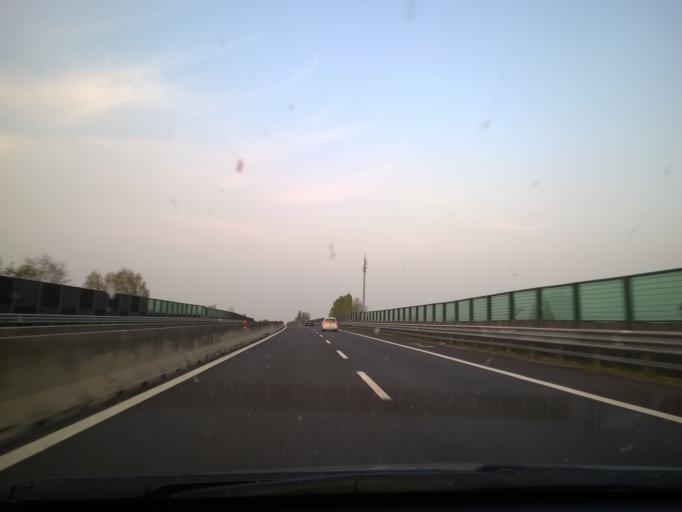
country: IT
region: Veneto
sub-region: Provincia di Padova
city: Masera di Padova
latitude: 45.3395
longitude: 11.8642
